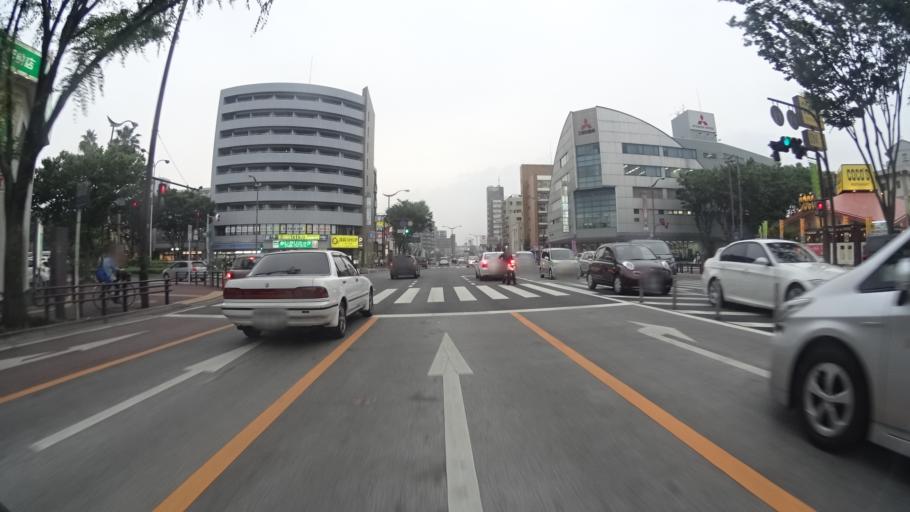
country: JP
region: Fukuoka
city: Fukuoka-shi
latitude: 33.5598
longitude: 130.4280
